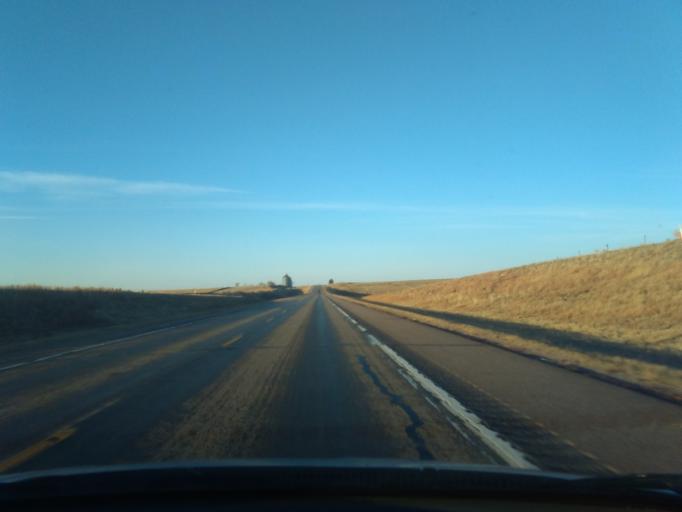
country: US
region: Nebraska
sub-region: Cheyenne County
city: Sidney
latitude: 41.2090
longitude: -102.9710
